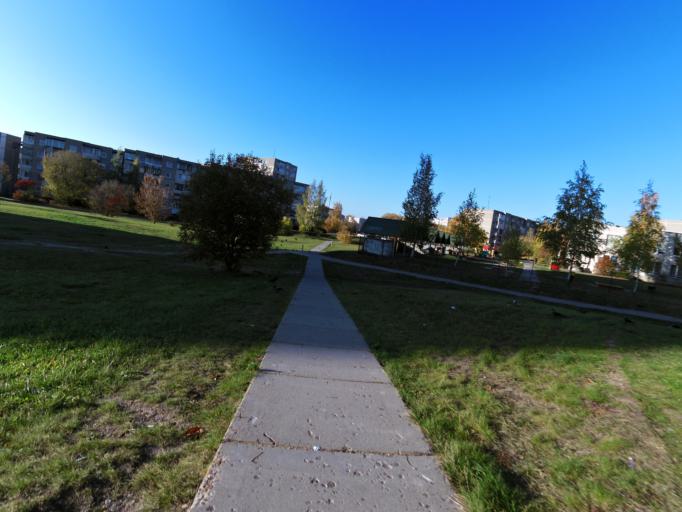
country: LT
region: Vilnius County
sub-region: Vilnius
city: Fabijoniskes
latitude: 54.7346
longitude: 25.2407
